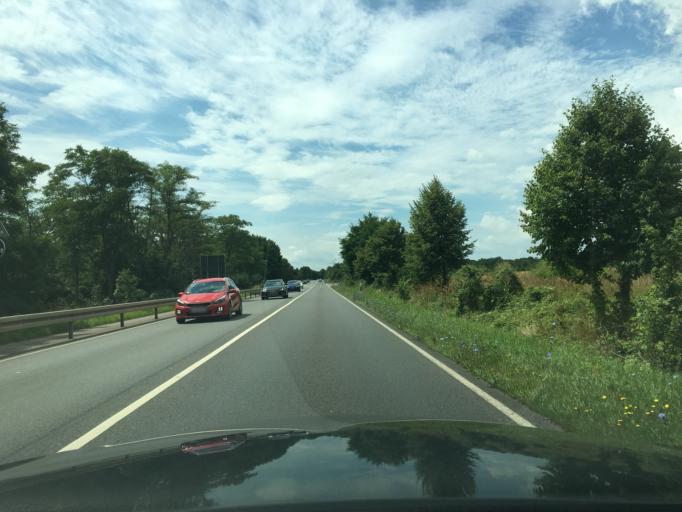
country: DE
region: Saxony-Anhalt
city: Zscherndorf
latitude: 51.5971
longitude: 12.2784
